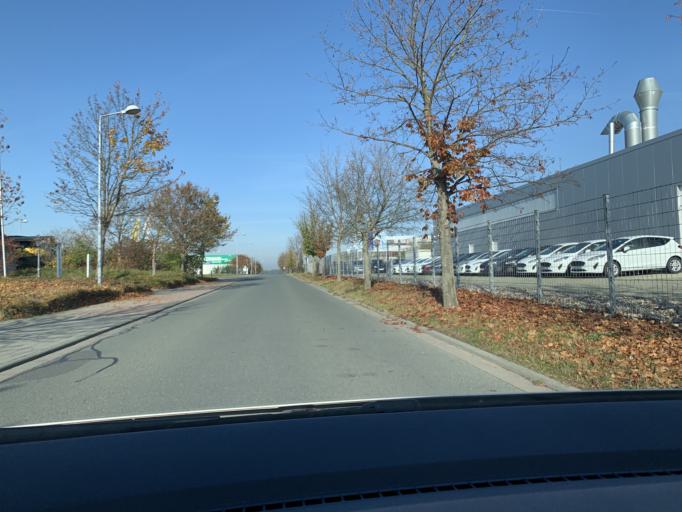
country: DE
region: Thuringia
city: Schmolln
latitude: 50.8827
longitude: 12.3498
